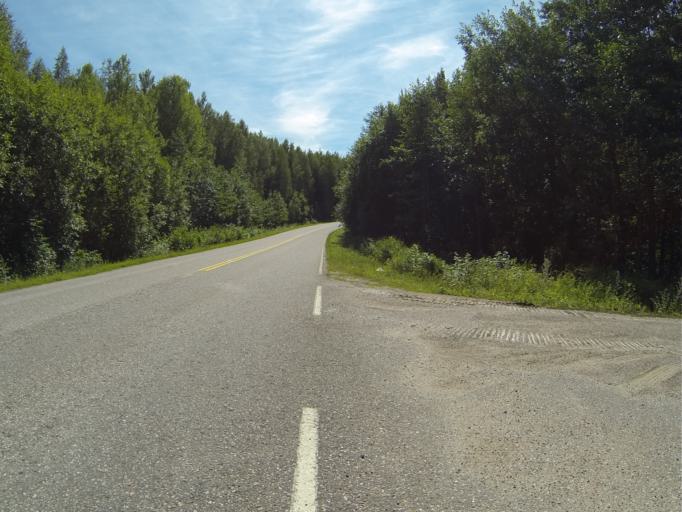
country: FI
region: Varsinais-Suomi
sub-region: Salo
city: Halikko
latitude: 60.2729
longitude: 22.9834
